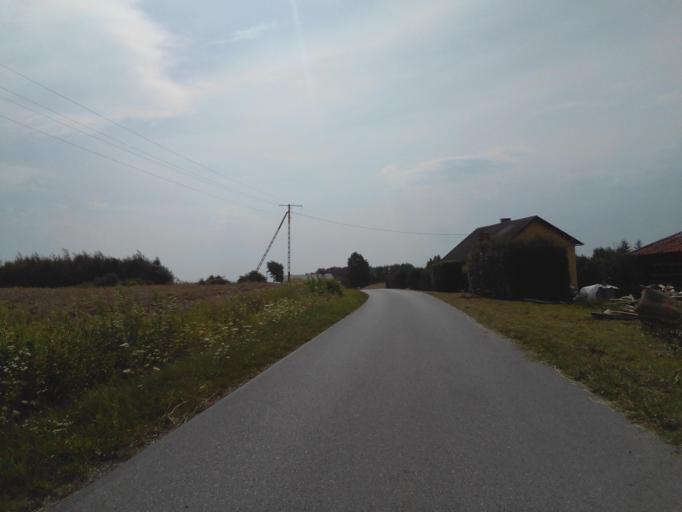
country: PL
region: Subcarpathian Voivodeship
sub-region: Powiat strzyzowski
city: Frysztak
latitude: 49.8658
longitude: 21.5309
